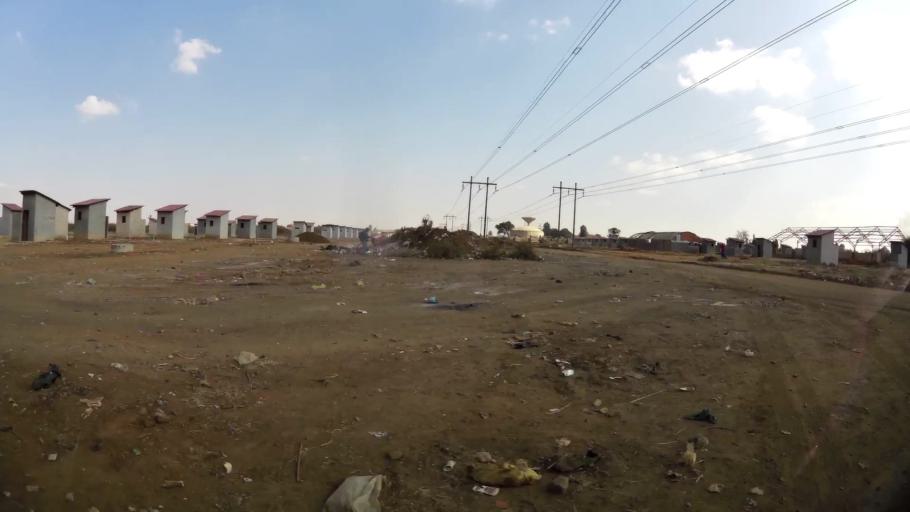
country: ZA
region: Gauteng
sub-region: Ekurhuleni Metropolitan Municipality
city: Benoni
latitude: -26.1416
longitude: 28.4070
